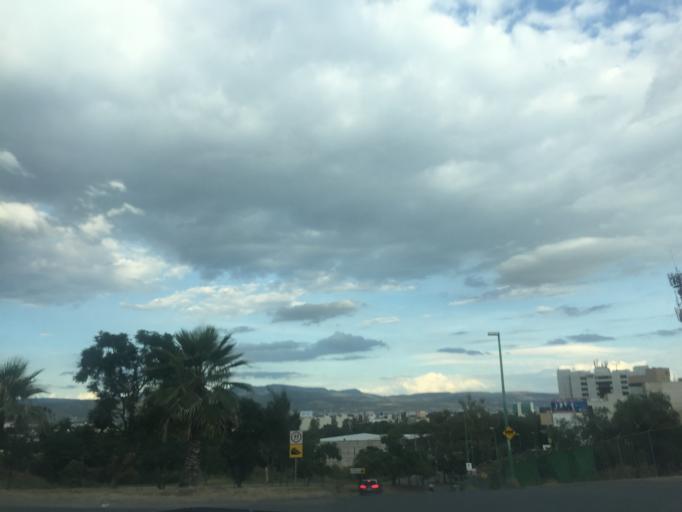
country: MX
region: Guanajuato
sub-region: Leon
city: La Ermita
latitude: 21.1549
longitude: -101.7021
